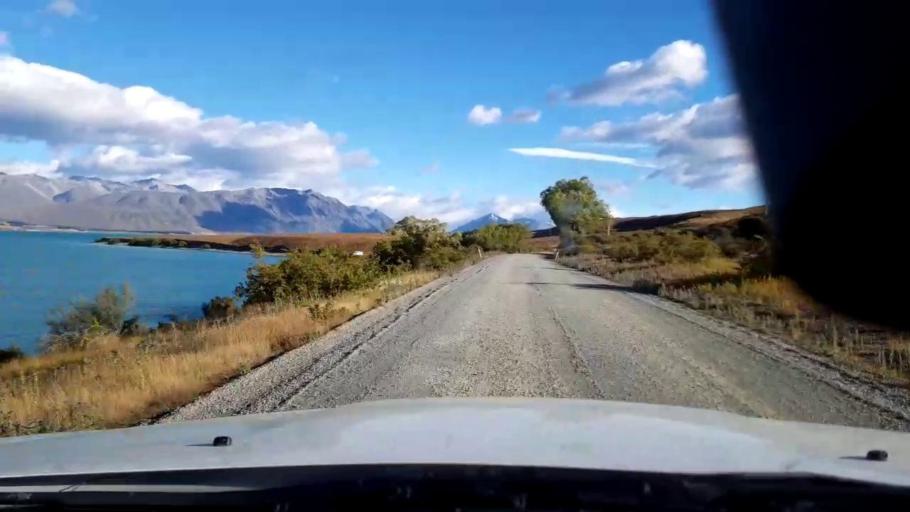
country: NZ
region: Canterbury
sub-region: Timaru District
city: Pleasant Point
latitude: -43.9282
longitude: 170.5603
